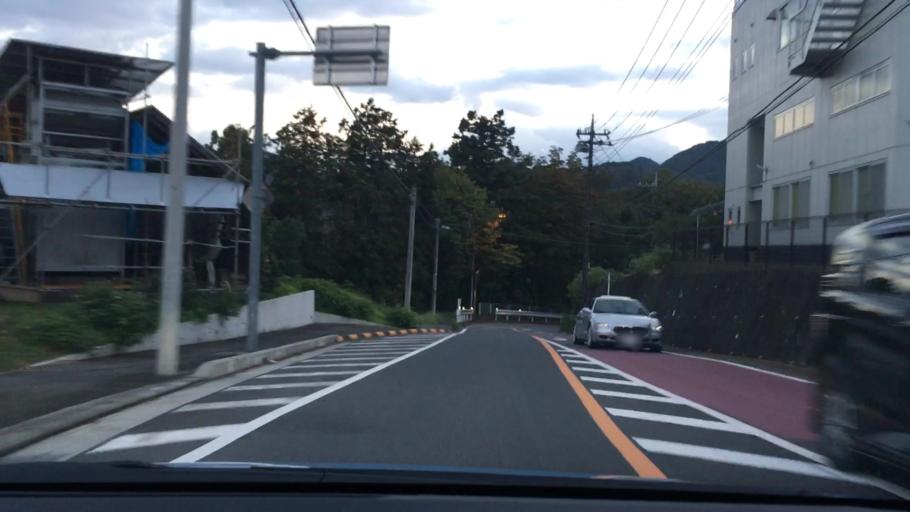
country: JP
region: Tokyo
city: Hachioji
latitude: 35.5740
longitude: 139.2759
